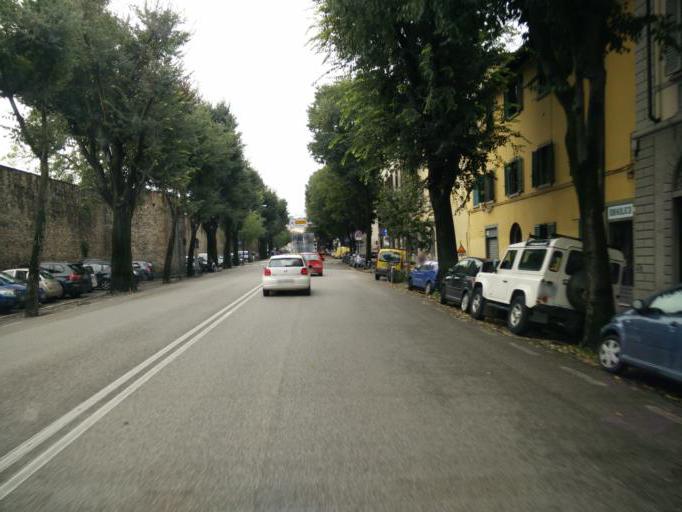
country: IT
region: Tuscany
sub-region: Province of Florence
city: Florence
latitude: 43.7632
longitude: 11.2411
